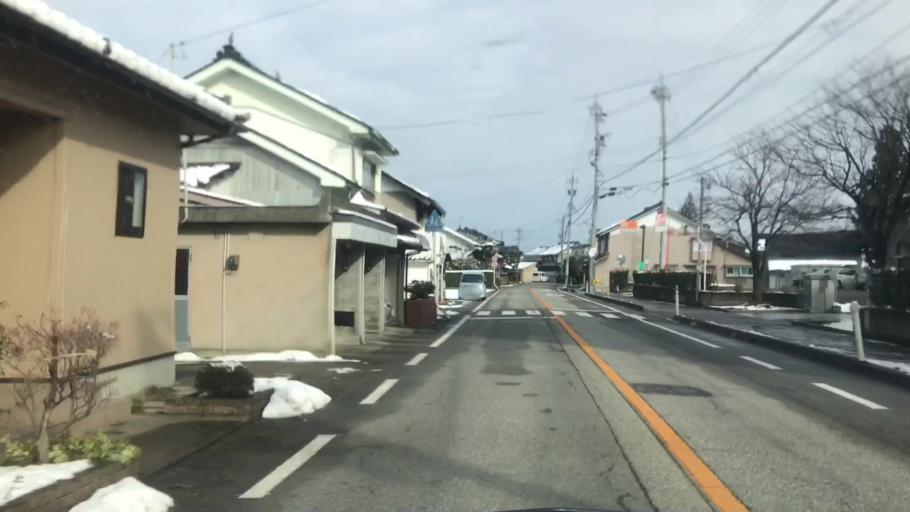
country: JP
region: Toyama
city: Toyama-shi
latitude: 36.6227
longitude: 137.2523
